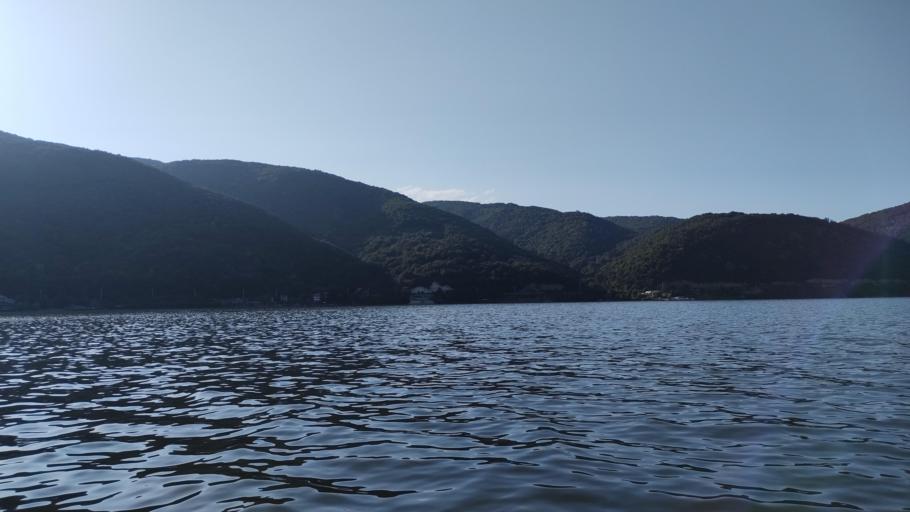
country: RO
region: Mehedinti
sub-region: Comuna Dubova
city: Dubova
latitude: 44.5738
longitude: 22.2433
